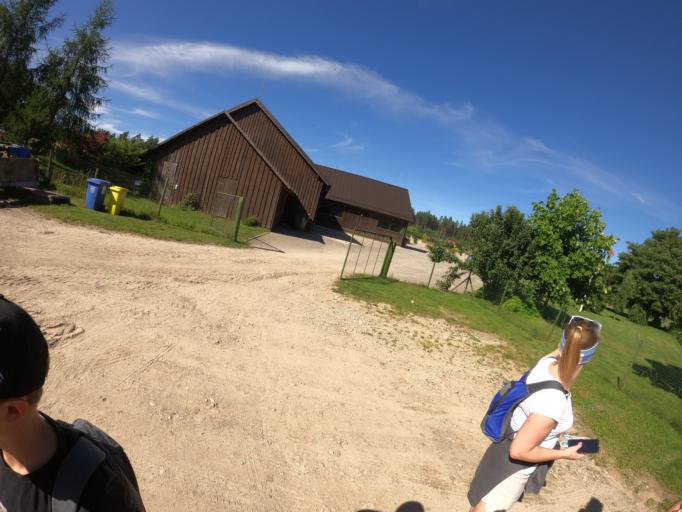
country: LT
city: Kelme
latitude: 55.8041
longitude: 22.9939
